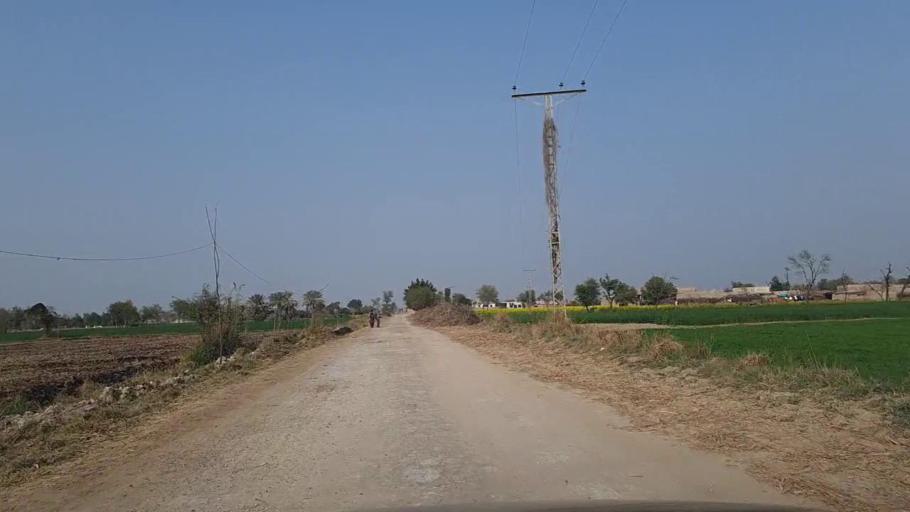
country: PK
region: Sindh
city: Daur
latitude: 26.4066
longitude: 68.4240
